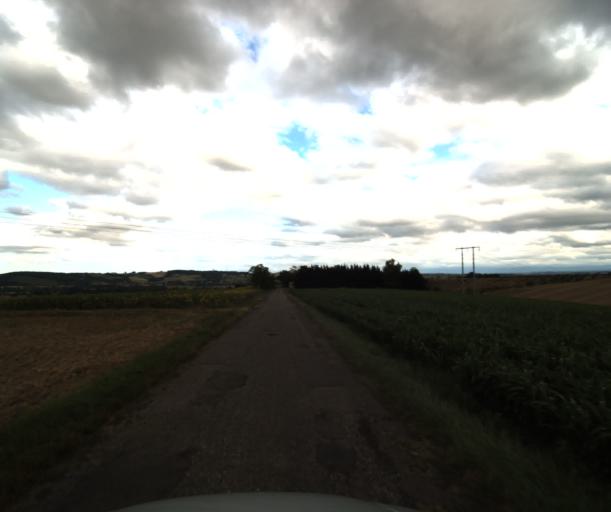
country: FR
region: Midi-Pyrenees
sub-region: Departement de la Haute-Garonne
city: Beaumont-sur-Leze
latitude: 43.3927
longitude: 1.3296
